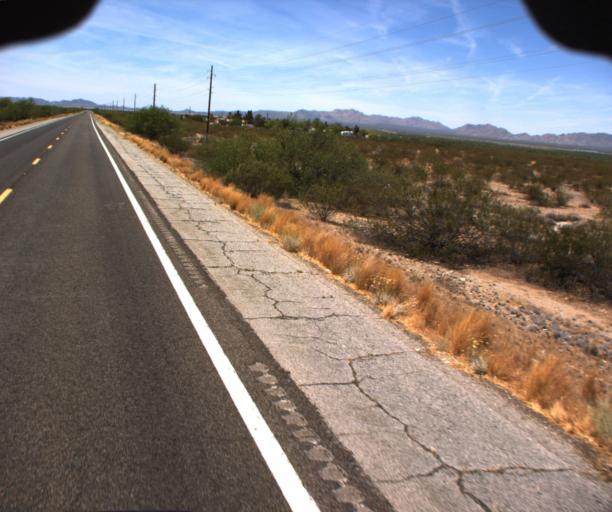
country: US
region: Arizona
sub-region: La Paz County
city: Salome
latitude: 33.8369
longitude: -113.4895
